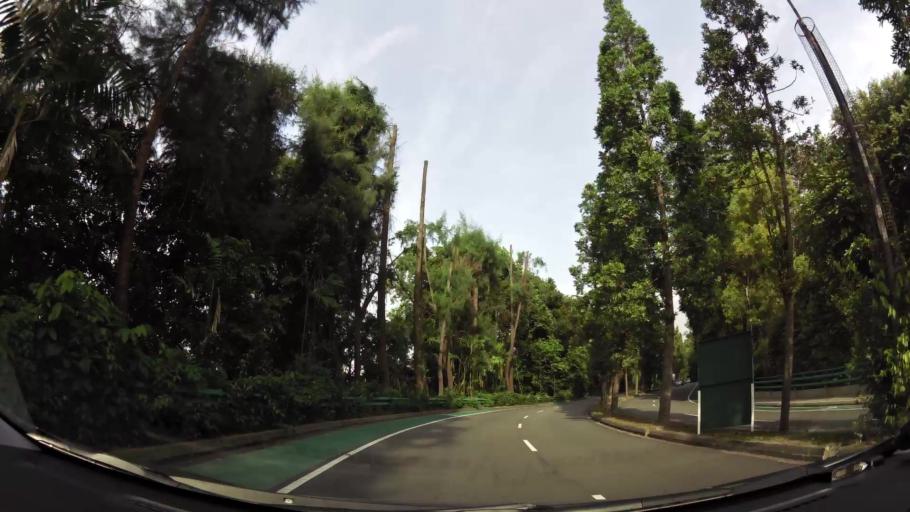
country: SG
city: Singapore
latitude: 1.2464
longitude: 103.8345
